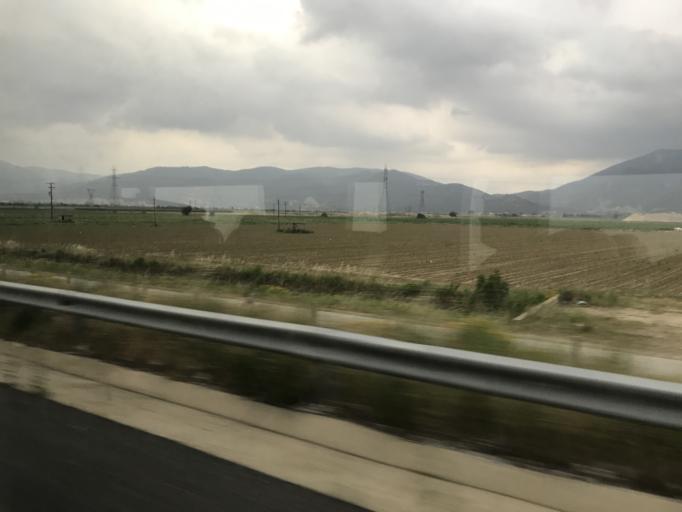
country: GR
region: East Macedonia and Thrace
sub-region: Nomos Rodopis
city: Iasmos
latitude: 41.1120
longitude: 25.2241
